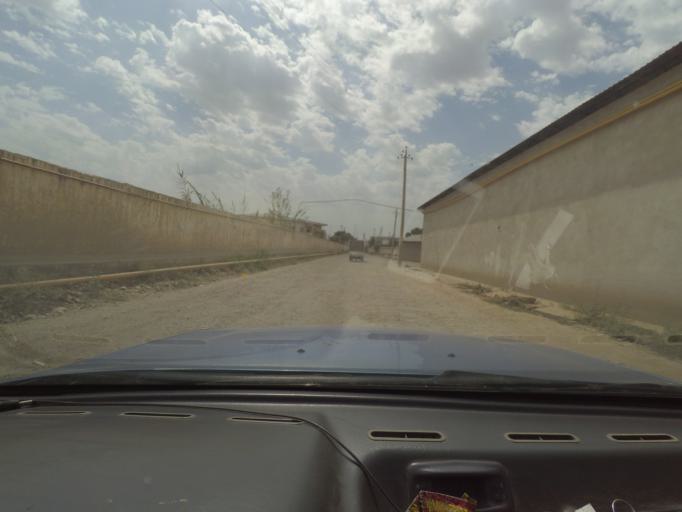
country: UZ
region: Toshkent
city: Urtaowul
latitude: 41.2333
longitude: 69.1534
